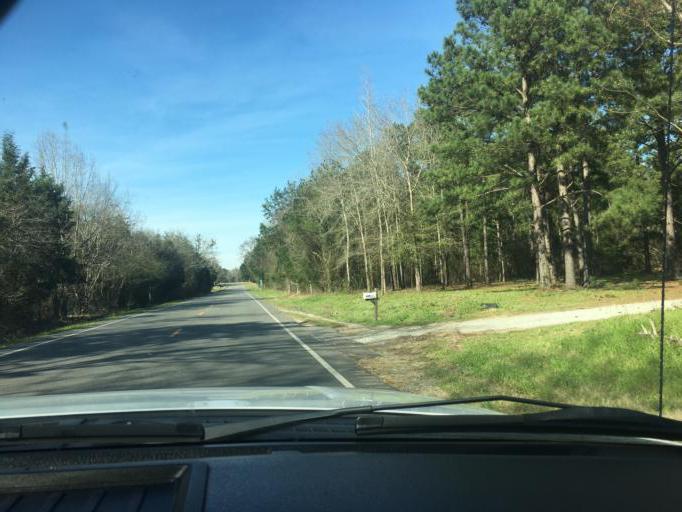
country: US
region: Alabama
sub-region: Lee County
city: Opelika
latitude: 32.4613
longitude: -85.3683
